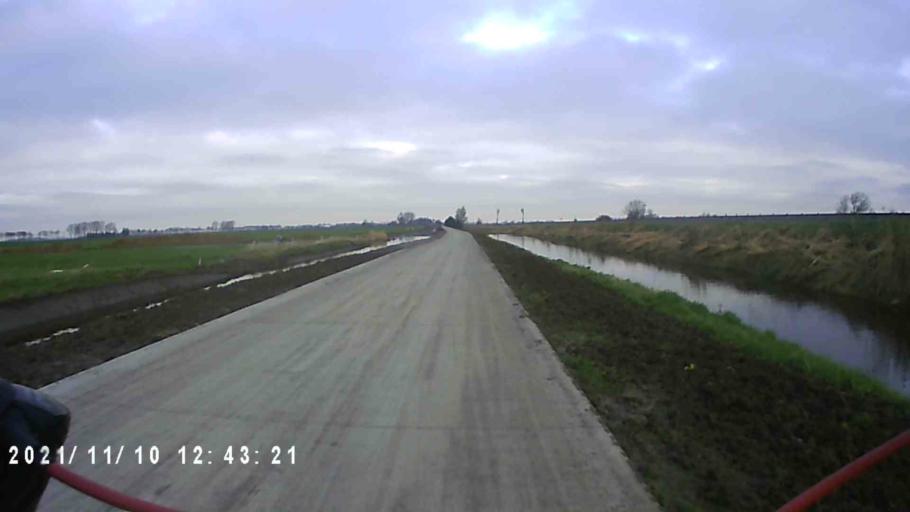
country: NL
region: Groningen
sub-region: Gemeente Groningen
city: Korrewegwijk
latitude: 53.2531
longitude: 6.5514
